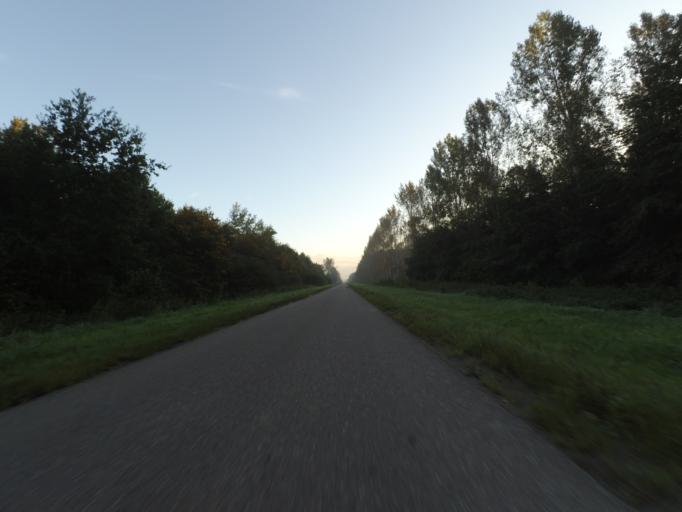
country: NL
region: Flevoland
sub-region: Gemeente Zeewolde
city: Zeewolde
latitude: 52.3402
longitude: 5.4699
